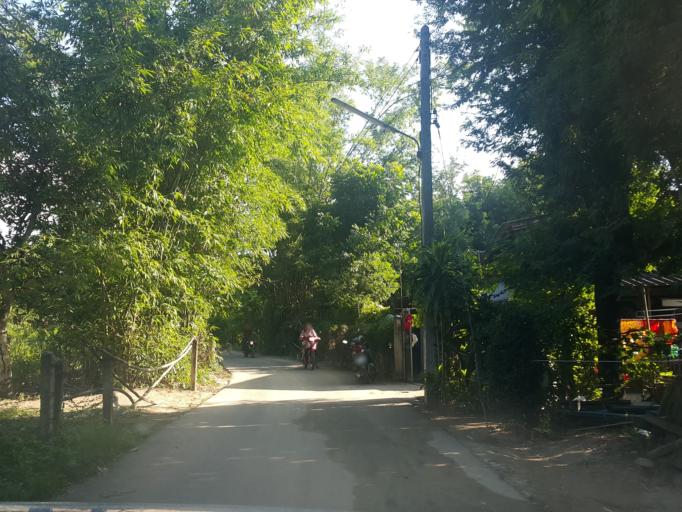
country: TH
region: Chiang Mai
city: Mae On
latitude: 18.7181
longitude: 99.2092
